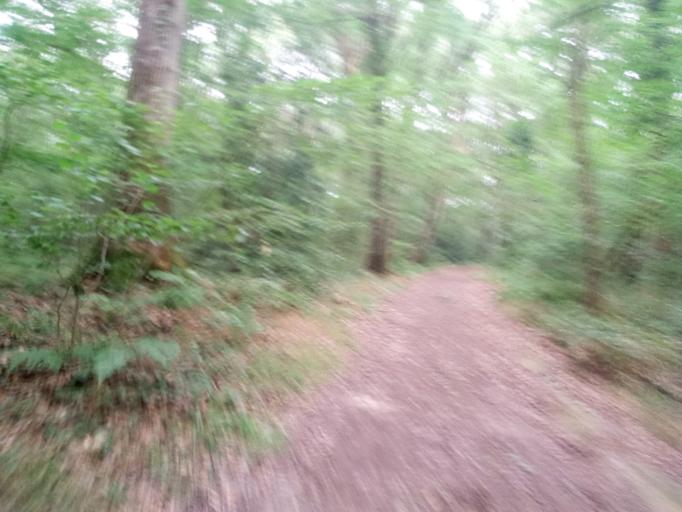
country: FR
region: Lower Normandy
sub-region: Departement du Calvados
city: Clinchamps-sur-Orne
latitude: 49.0480
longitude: -0.4380
